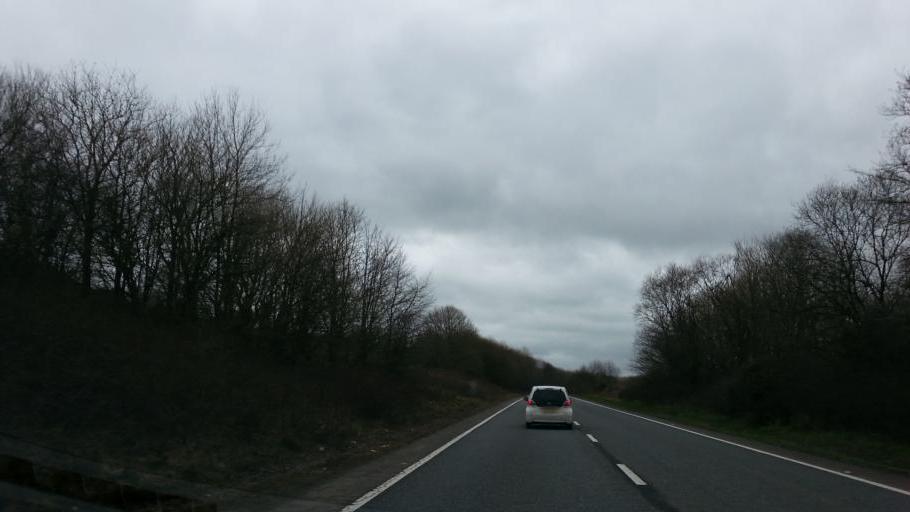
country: GB
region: England
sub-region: Devon
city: Tiverton
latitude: 50.9416
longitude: -3.5839
